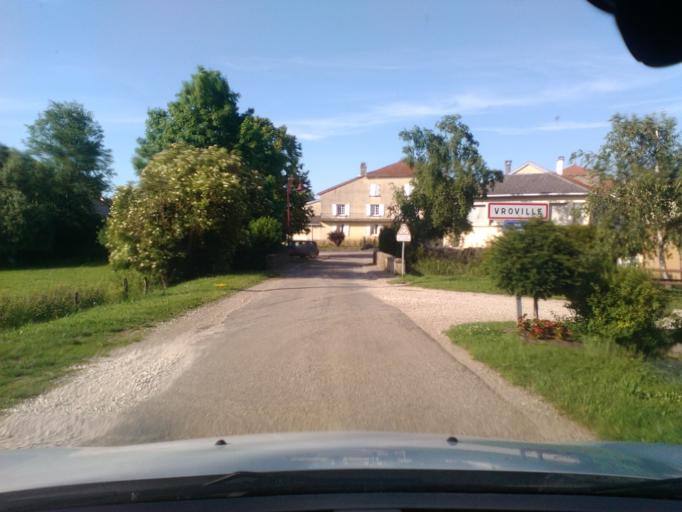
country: FR
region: Lorraine
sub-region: Departement des Vosges
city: Mirecourt
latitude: 48.2862
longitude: 6.1696
